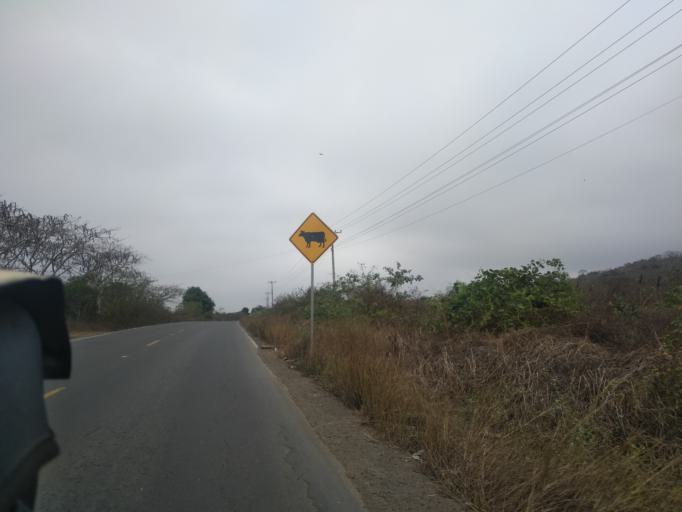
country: EC
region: Manabi
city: Montecristi
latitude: -1.0639
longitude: -80.6566
